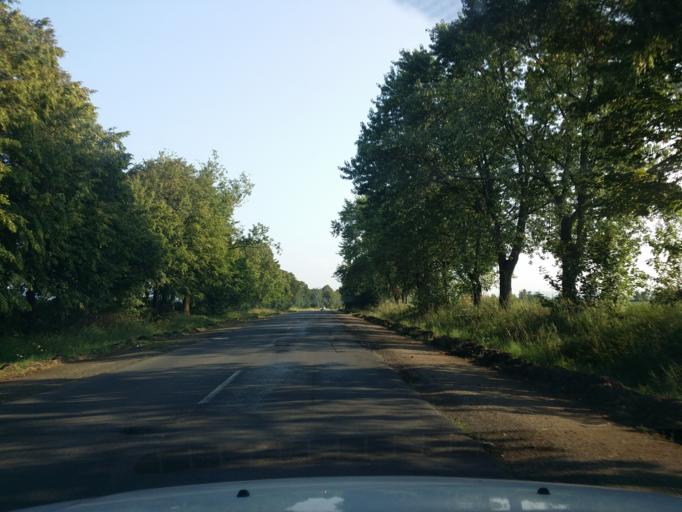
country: HU
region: Borsod-Abauj-Zemplen
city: Abaujszanto
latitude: 48.3586
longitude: 21.2153
